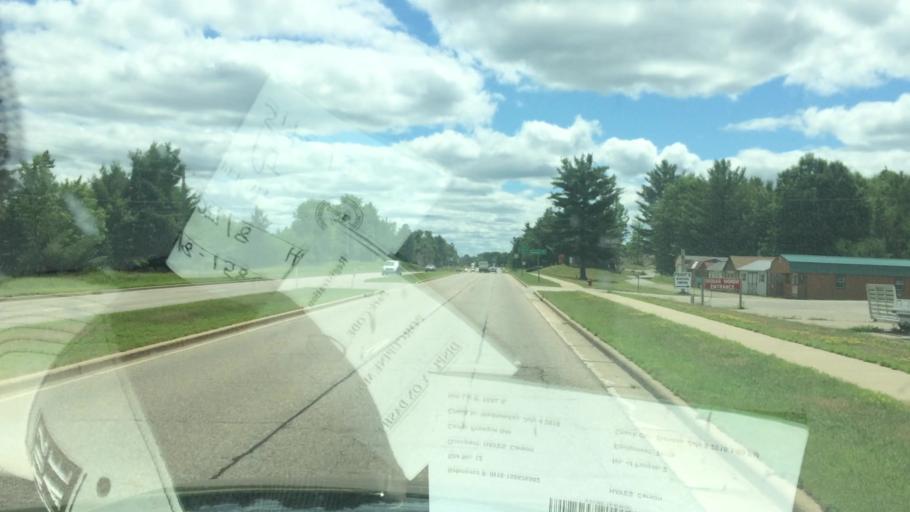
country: US
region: Wisconsin
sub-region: Oneida County
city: Rhinelander
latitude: 45.6533
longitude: -89.3817
